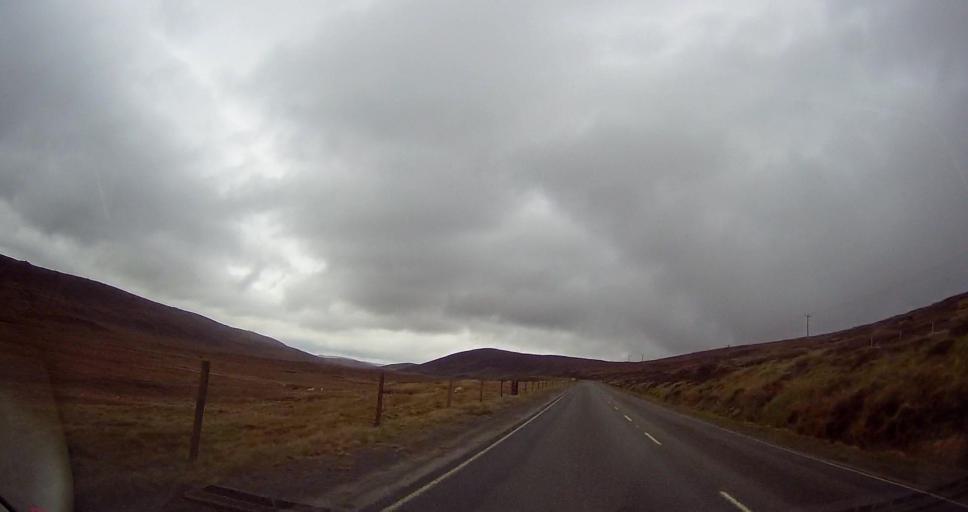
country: GB
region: Scotland
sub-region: Shetland Islands
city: Lerwick
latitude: 60.2903
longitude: -1.2405
